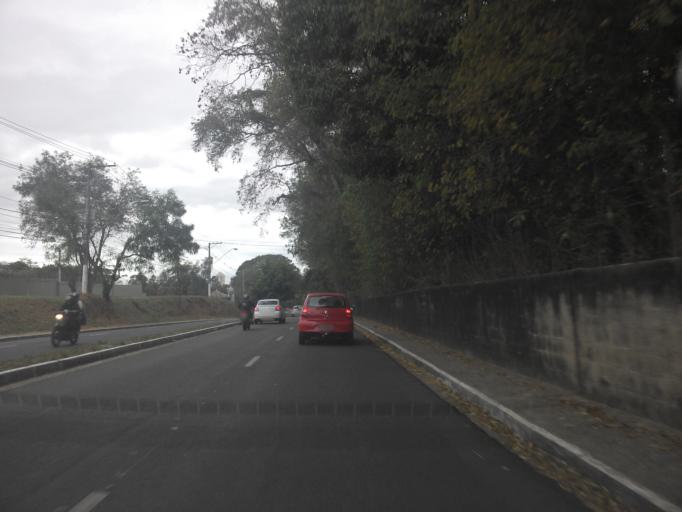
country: BR
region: Sao Paulo
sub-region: Taubate
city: Taubate
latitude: -23.0268
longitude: -45.6010
